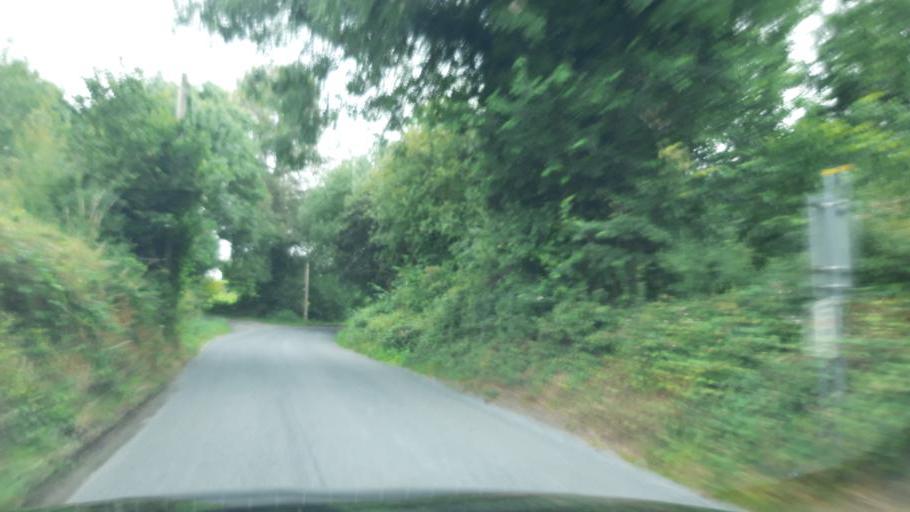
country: IE
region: Leinster
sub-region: Kilkenny
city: Ballyragget
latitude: 52.7233
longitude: -7.4004
